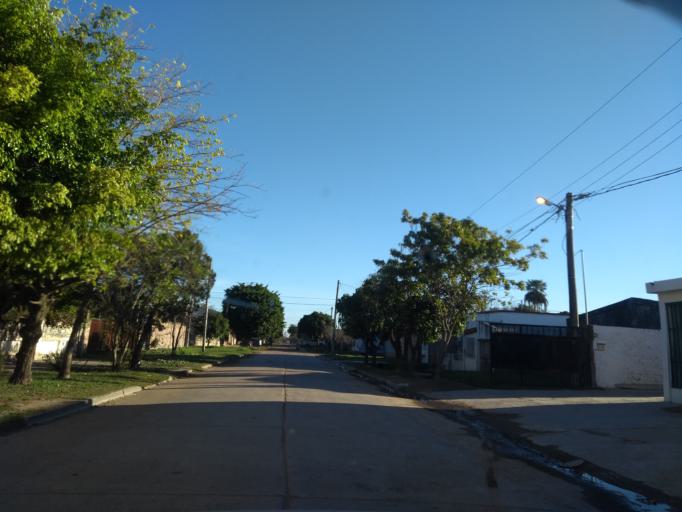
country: AR
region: Chaco
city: Barranqueras
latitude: -27.4872
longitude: -58.9322
